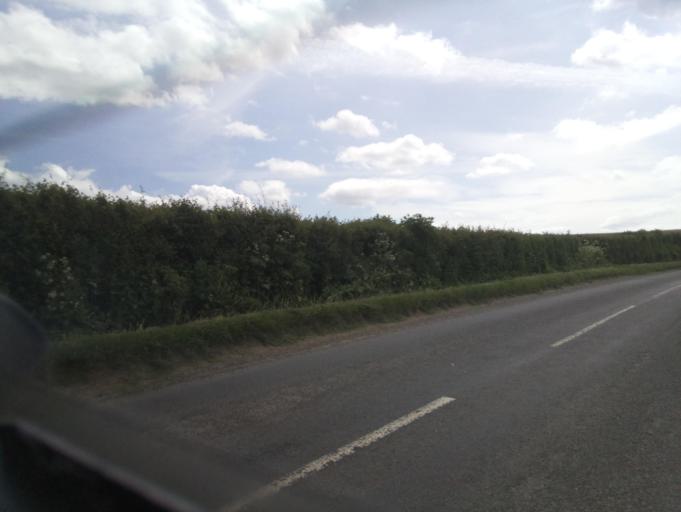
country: GB
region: England
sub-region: Herefordshire
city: Pencoyd
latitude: 51.9100
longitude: -2.6956
